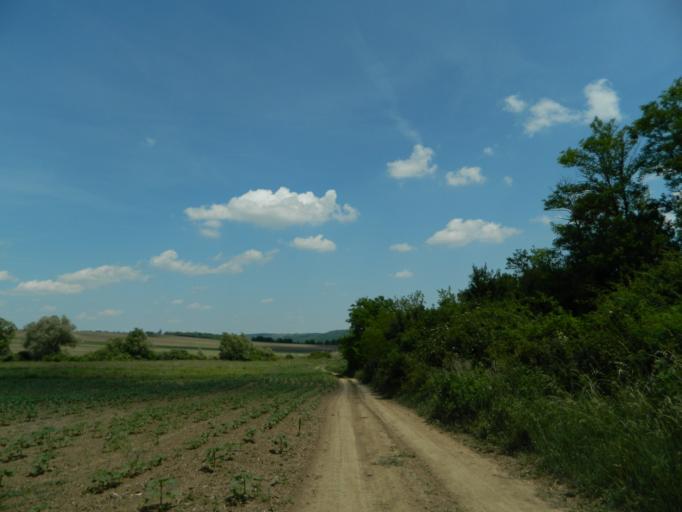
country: HU
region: Somogy
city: Tab
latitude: 46.7578
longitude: 17.9586
